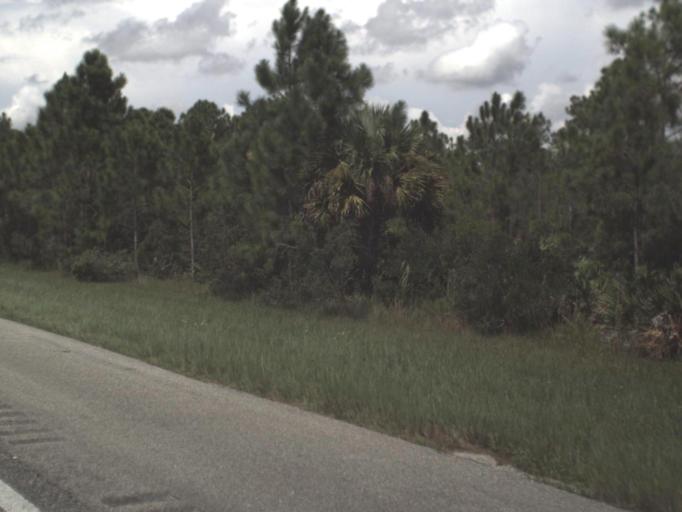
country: US
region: Florida
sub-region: Lee County
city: Suncoast Estates
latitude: 26.7750
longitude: -81.8863
